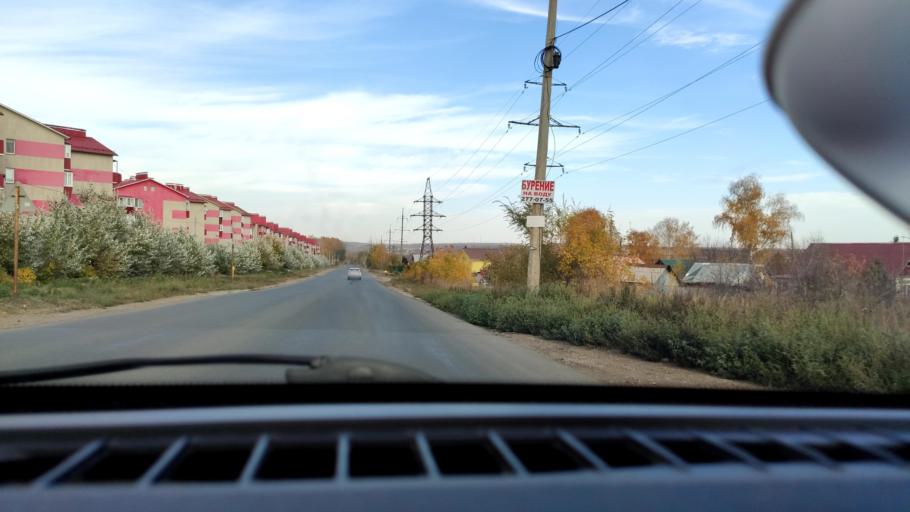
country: RU
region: Samara
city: Novosemeykino
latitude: 53.3289
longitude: 50.3126
